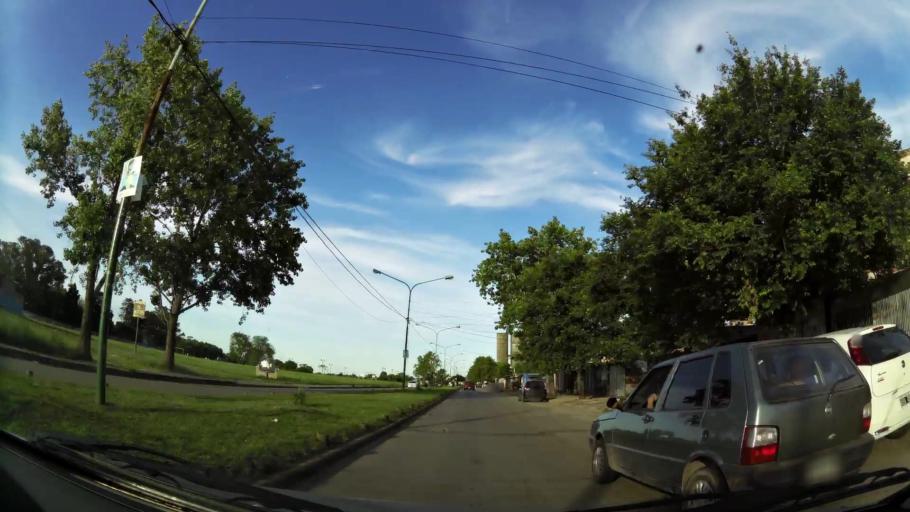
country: AR
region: Buenos Aires
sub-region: Partido de Almirante Brown
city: Adrogue
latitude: -34.8186
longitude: -58.3412
